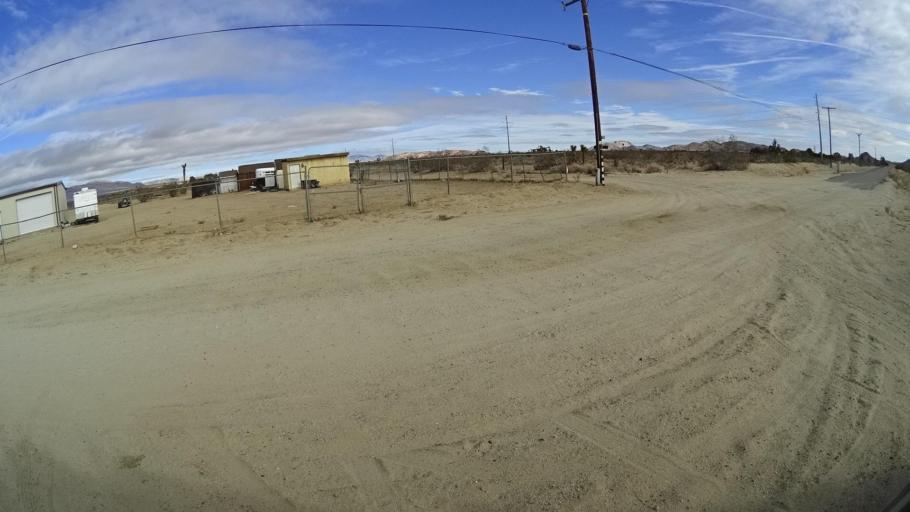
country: US
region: California
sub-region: Kern County
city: Rosamond
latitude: 34.8924
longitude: -118.3180
